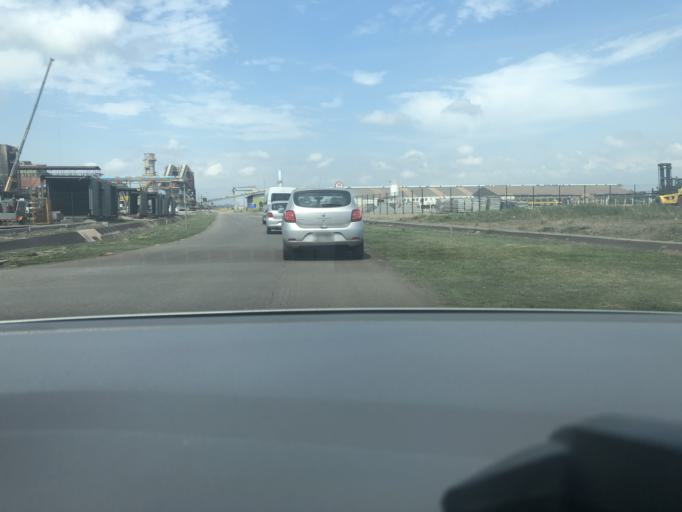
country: BR
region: Rio de Janeiro
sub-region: Itaguai
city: Itaguai
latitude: -22.9130
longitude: -43.7422
